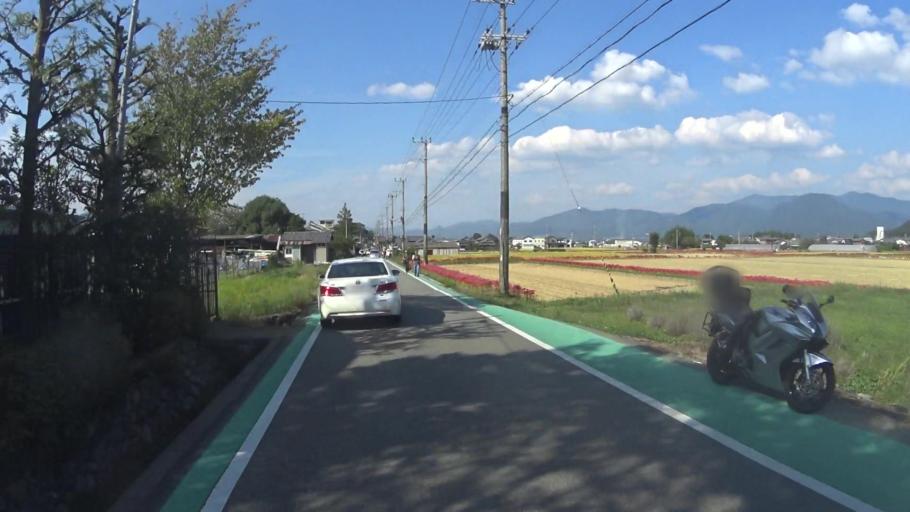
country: JP
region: Kyoto
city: Kameoka
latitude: 35.0016
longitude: 135.5494
